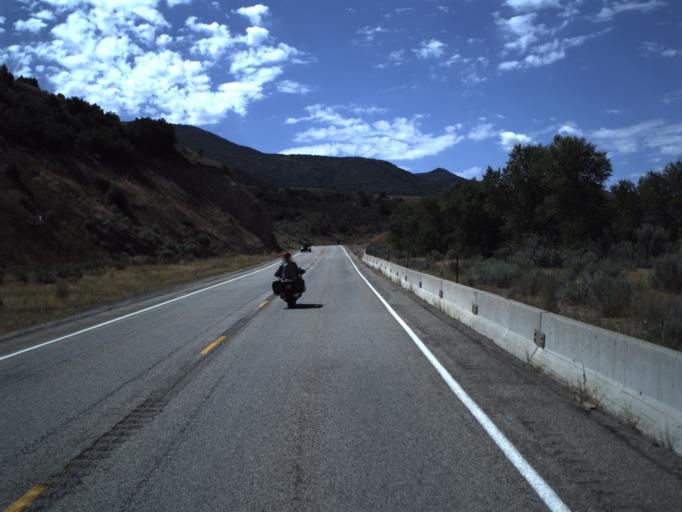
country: US
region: Utah
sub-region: Utah County
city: Woodland Hills
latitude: 39.9788
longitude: -111.5032
